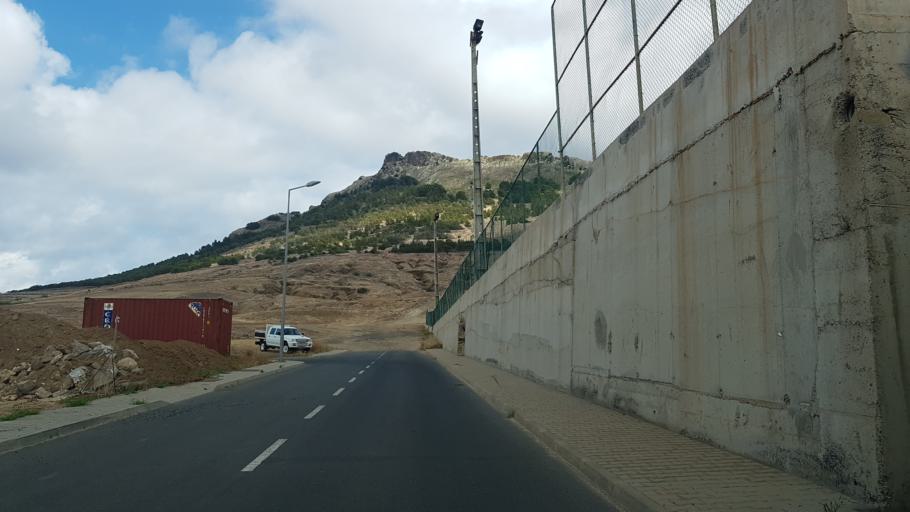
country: PT
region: Madeira
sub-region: Porto Santo
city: Vila de Porto Santo
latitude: 33.0438
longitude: -16.3603
